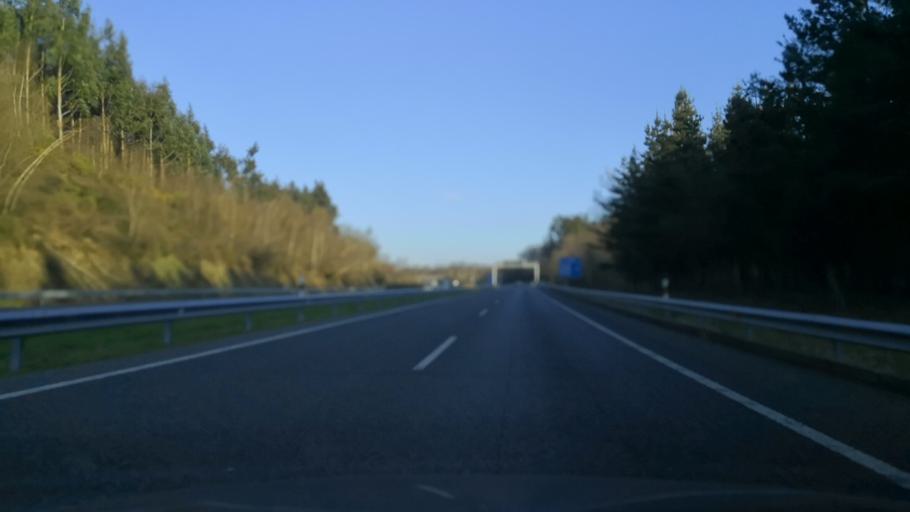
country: ES
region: Galicia
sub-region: Provincia de Lugo
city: O Paramo
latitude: 42.9089
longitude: -7.3053
